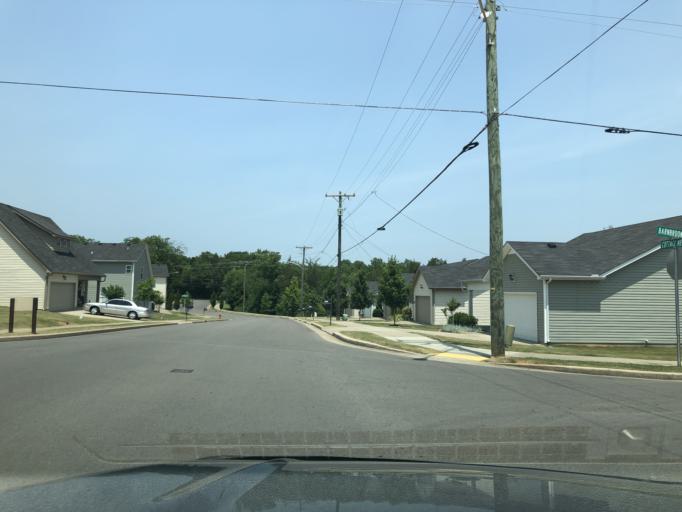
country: US
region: Tennessee
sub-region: Rutherford County
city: La Vergne
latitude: 36.0573
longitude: -86.6100
